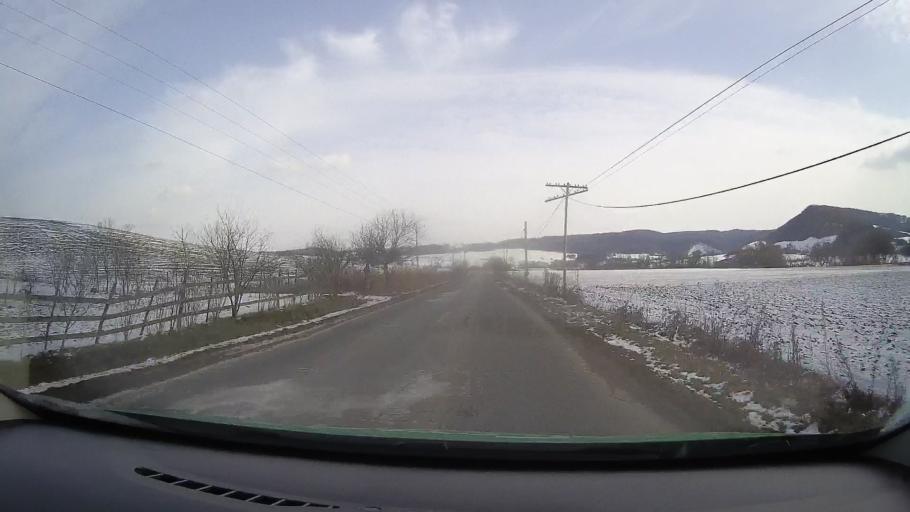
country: RO
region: Mures
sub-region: Comuna Apold
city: Saes
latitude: 46.1434
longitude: 24.7819
